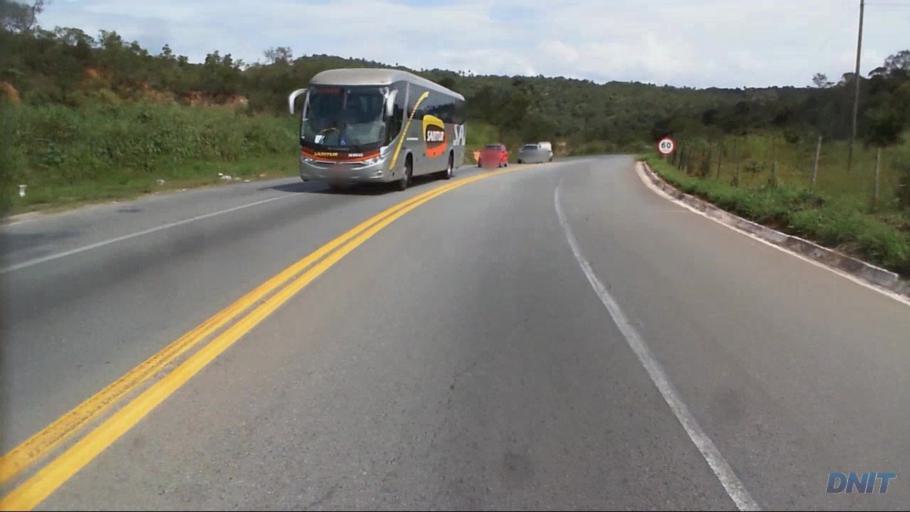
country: BR
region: Minas Gerais
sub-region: Santa Luzia
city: Santa Luzia
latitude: -19.8176
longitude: -43.8109
